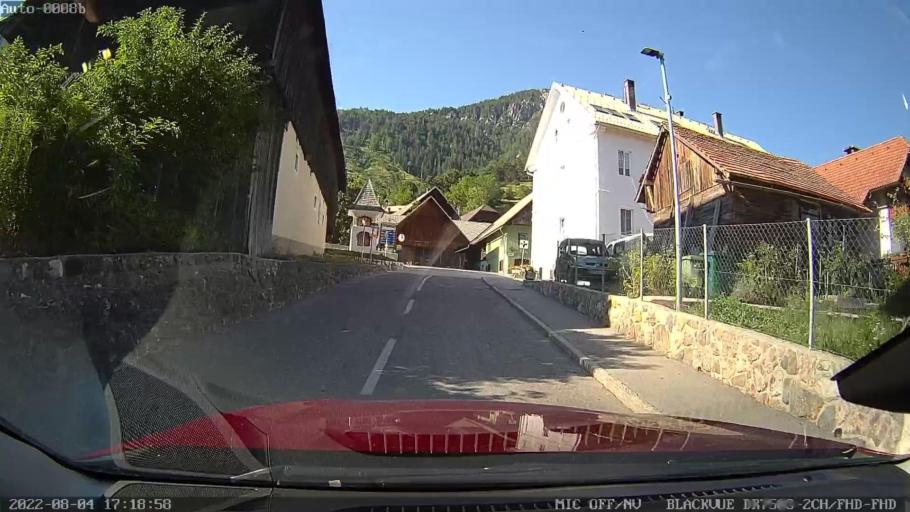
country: SI
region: Jesenice
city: Hrusica
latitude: 46.4669
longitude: 13.9462
